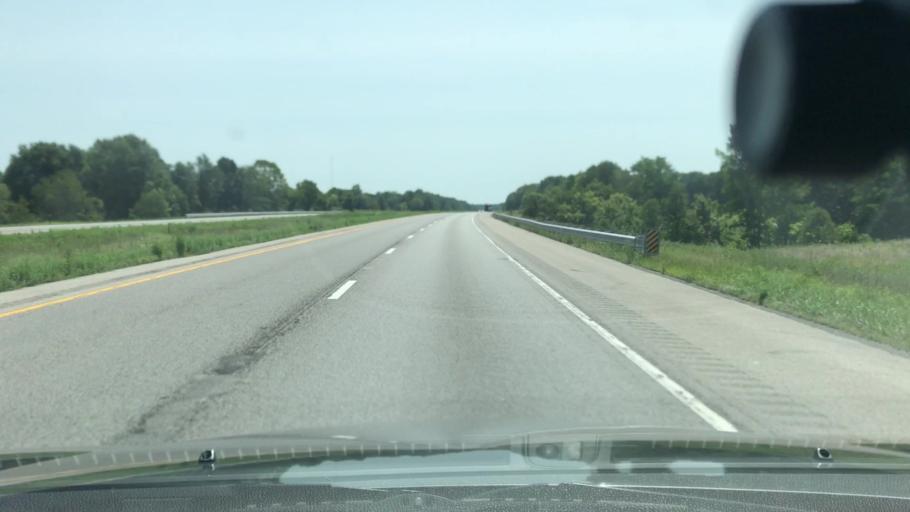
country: US
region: Illinois
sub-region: Clinton County
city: Wamac
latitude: 38.3769
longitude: -89.1053
